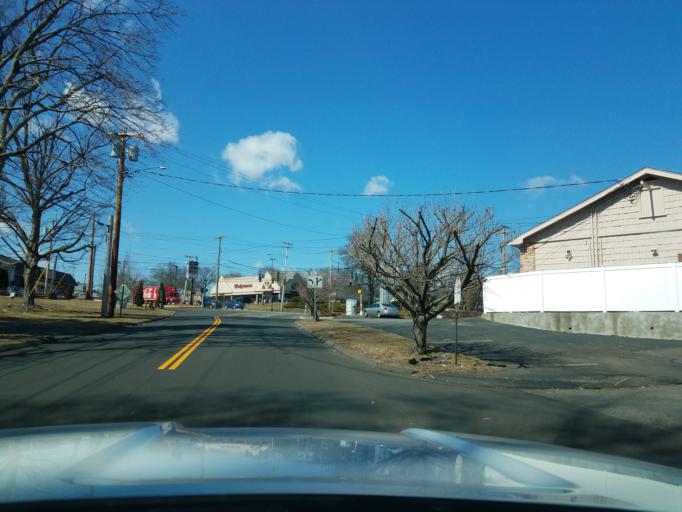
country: US
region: Connecticut
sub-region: Fairfield County
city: Stratford
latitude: 41.1950
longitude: -73.1402
